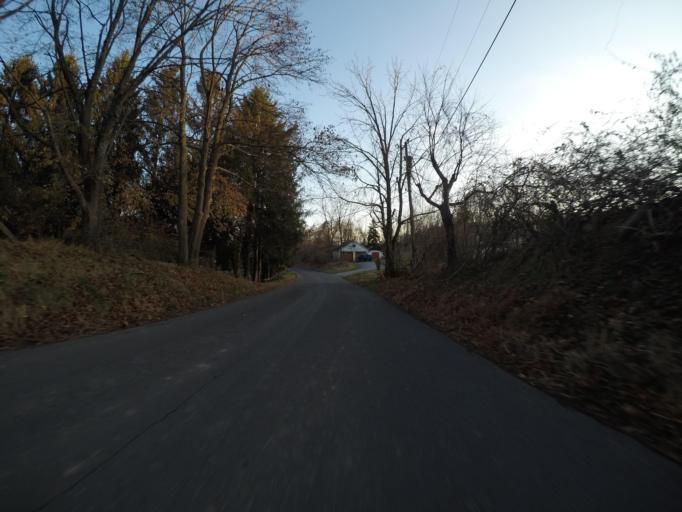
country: US
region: Maryland
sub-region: Carroll County
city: Hampstead
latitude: 39.5797
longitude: -76.8159
